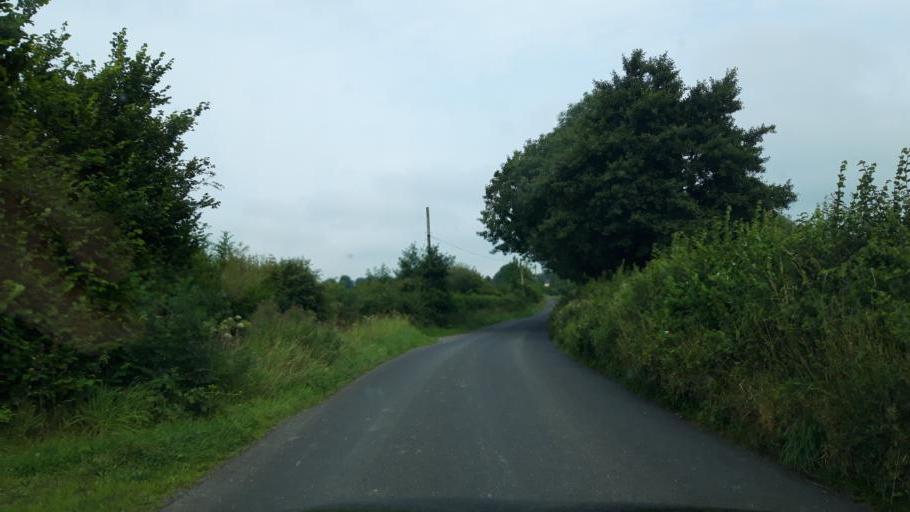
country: IE
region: Munster
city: Fethard
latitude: 52.5813
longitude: -7.5885
